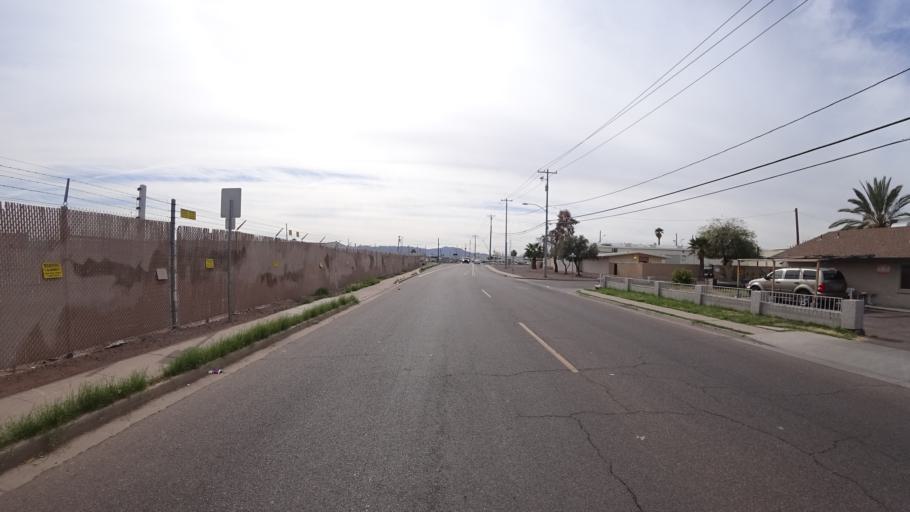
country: US
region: Arizona
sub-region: Maricopa County
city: Phoenix
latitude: 33.4451
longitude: -112.1260
